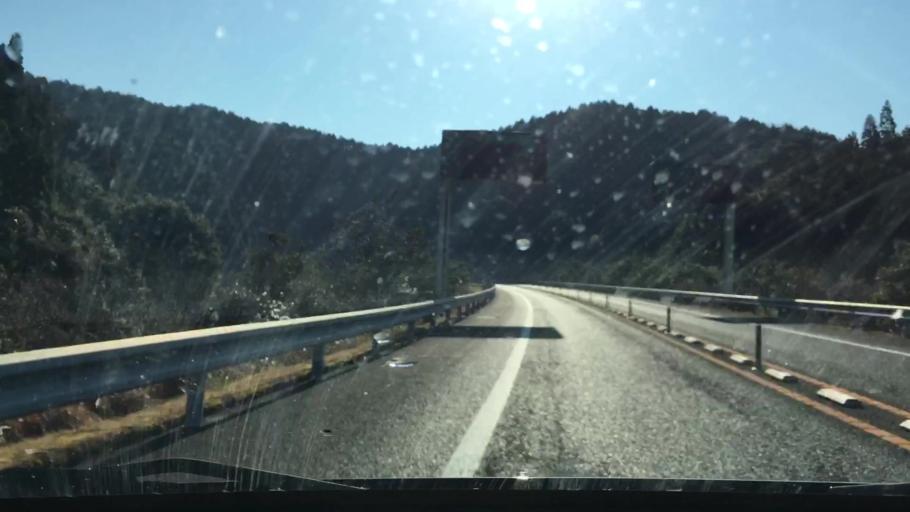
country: JP
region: Kagoshima
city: Kokubu-matsuki
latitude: 31.7269
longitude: 130.8406
